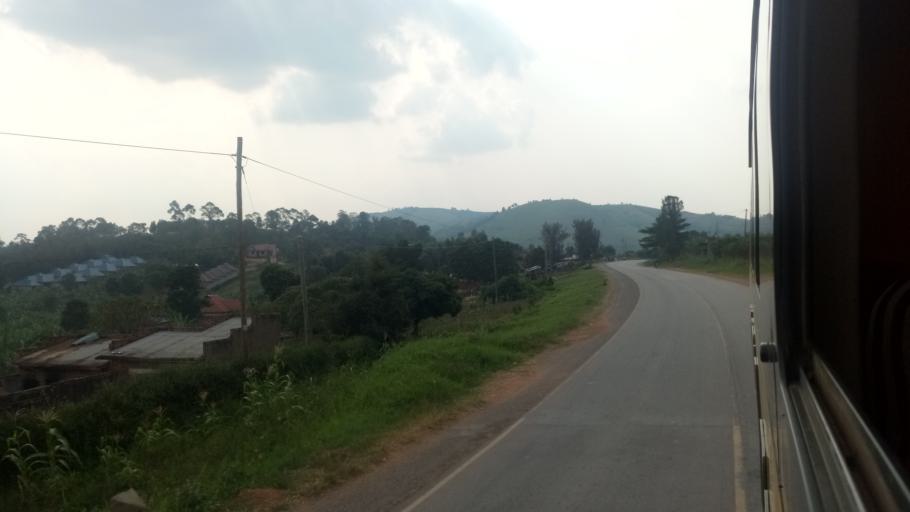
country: UG
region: Western Region
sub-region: Mbarara District
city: Mbarara
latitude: -0.5480
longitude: 30.7142
